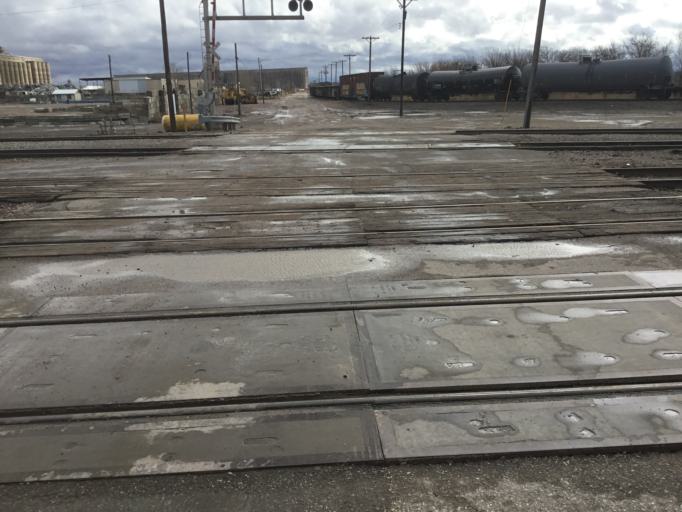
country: US
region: Kansas
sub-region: Sedgwick County
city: Wichita
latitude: 37.7299
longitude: -97.3356
